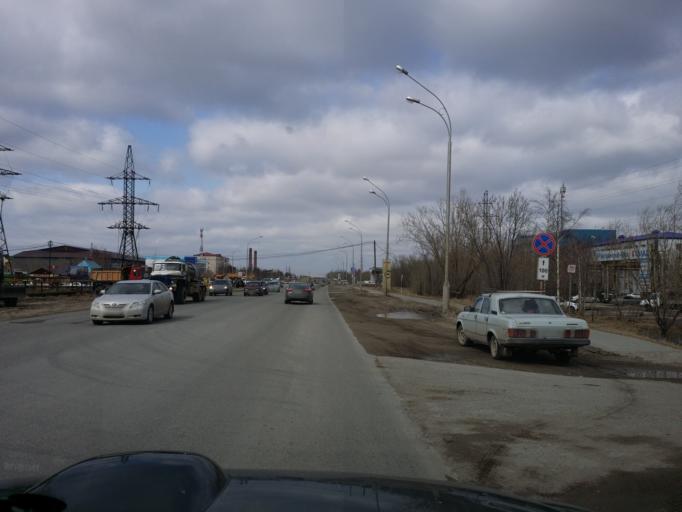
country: RU
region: Khanty-Mansiyskiy Avtonomnyy Okrug
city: Nizhnevartovsk
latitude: 60.9360
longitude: 76.5308
